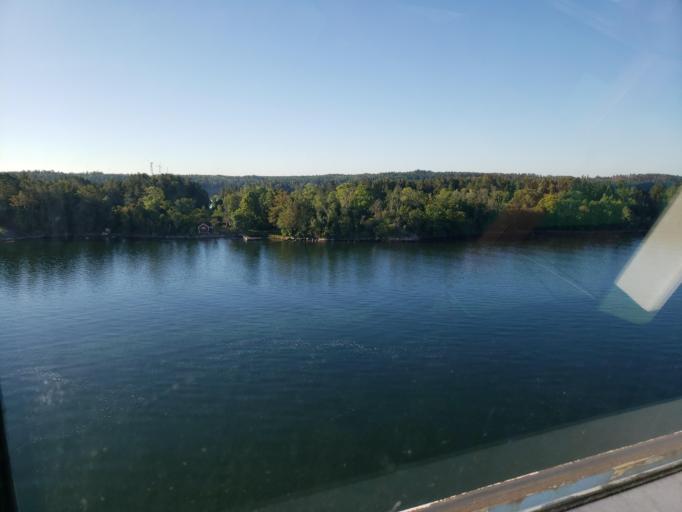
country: SE
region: Stockholm
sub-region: Varmdo Kommun
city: Hemmesta
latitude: 59.5394
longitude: 18.5705
